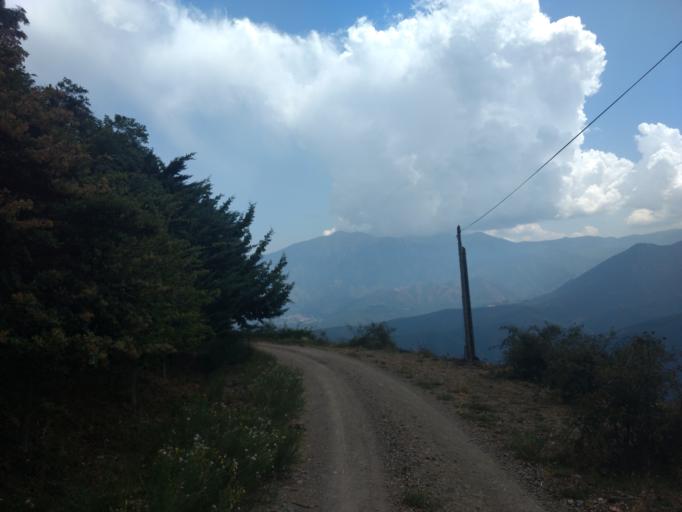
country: FR
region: Languedoc-Roussillon
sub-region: Departement des Pyrenees-Orientales
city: Vernet-les-Bains
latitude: 42.5760
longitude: 2.2884
